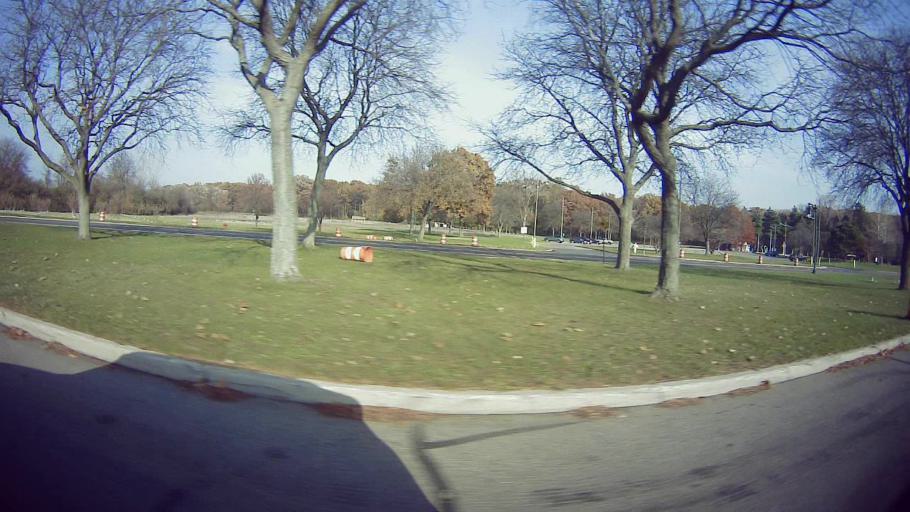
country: US
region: Michigan
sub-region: Wayne County
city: Highland Park
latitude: 42.4223
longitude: -83.1194
